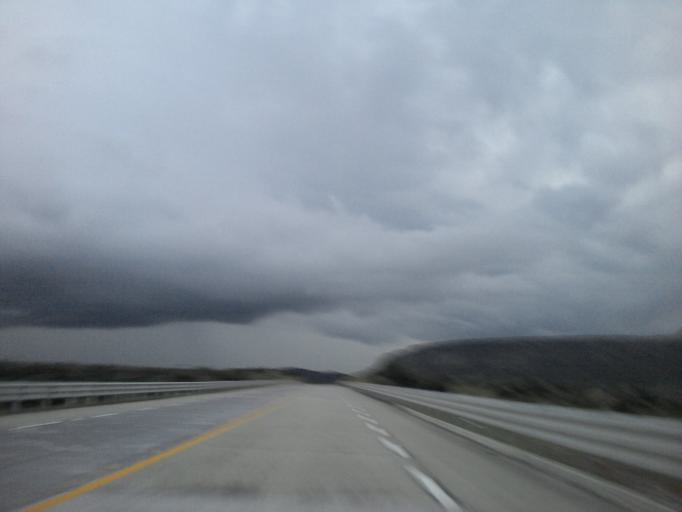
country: MX
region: Zacatecas
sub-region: Cuauhtemoc
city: Piedra Gorda
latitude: 22.5888
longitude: -102.3994
